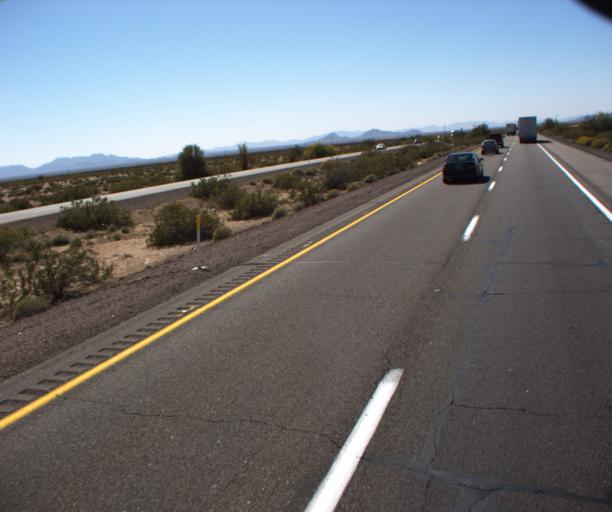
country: US
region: Arizona
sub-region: Yuma County
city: Wellton
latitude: 32.7180
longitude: -113.7931
